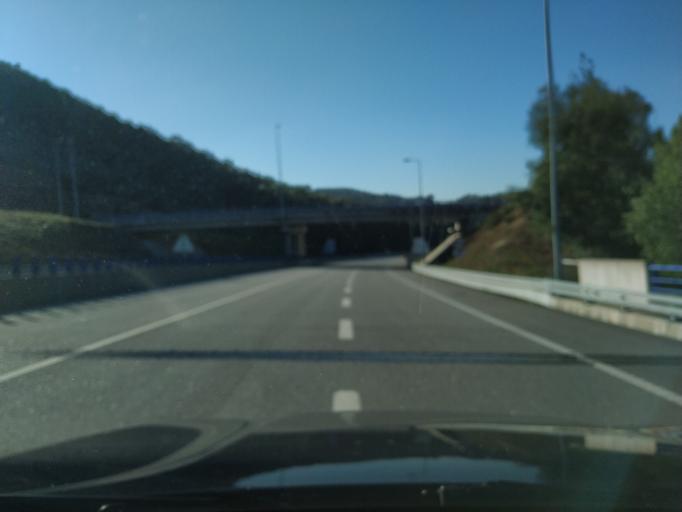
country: PT
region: Aveiro
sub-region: Oliveira de Azemeis
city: Vila Cha
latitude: 40.8755
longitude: -8.4319
